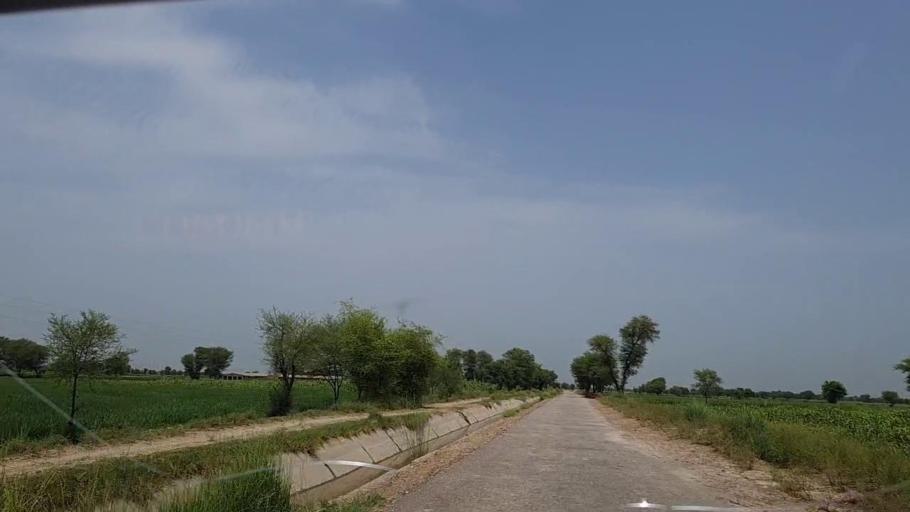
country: PK
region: Sindh
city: Tharu Shah
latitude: 26.9342
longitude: 68.0683
